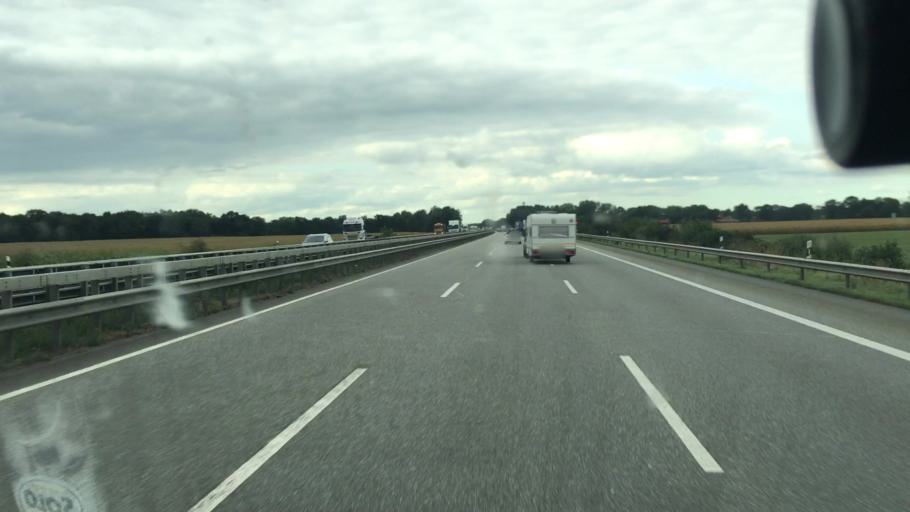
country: DE
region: Lower Saxony
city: Dinklage
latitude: 52.6815
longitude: 8.1721
